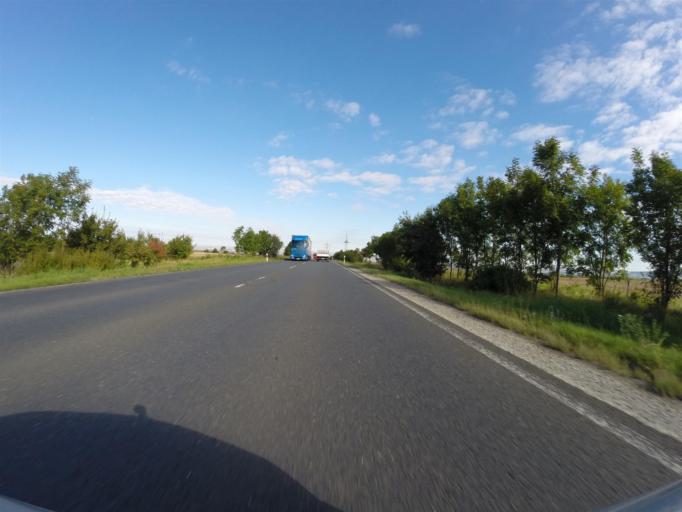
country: DE
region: Thuringia
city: Monchenholzhausen
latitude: 50.9505
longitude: 11.1704
